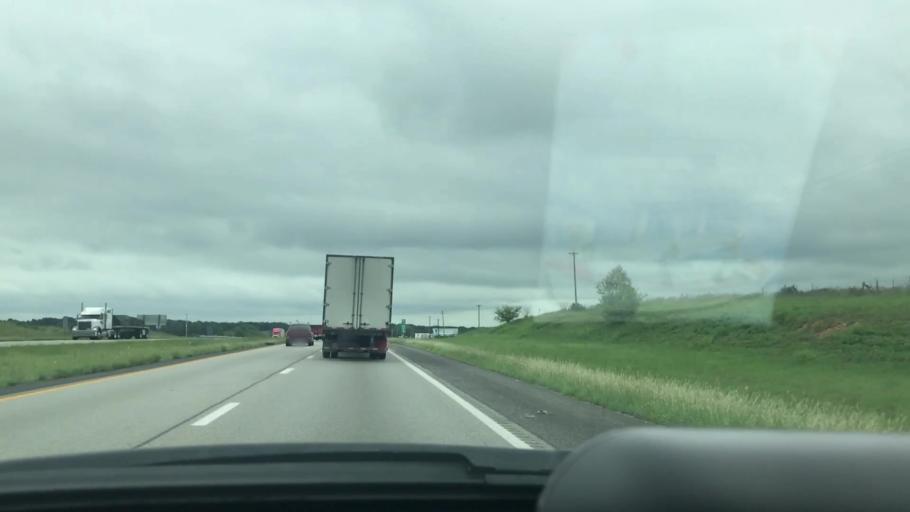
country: US
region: Missouri
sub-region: Christian County
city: Billings
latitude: 37.1853
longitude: -93.5916
